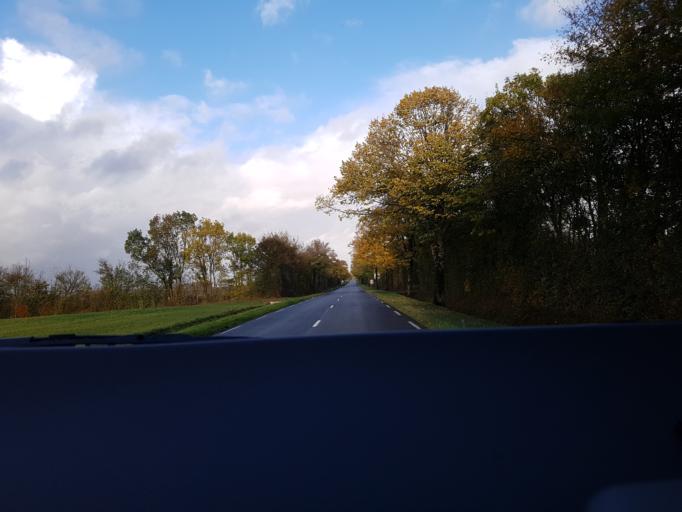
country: FR
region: Poitou-Charentes
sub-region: Departement des Deux-Sevres
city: Brioux-sur-Boutonne
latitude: 46.1115
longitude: -0.2532
